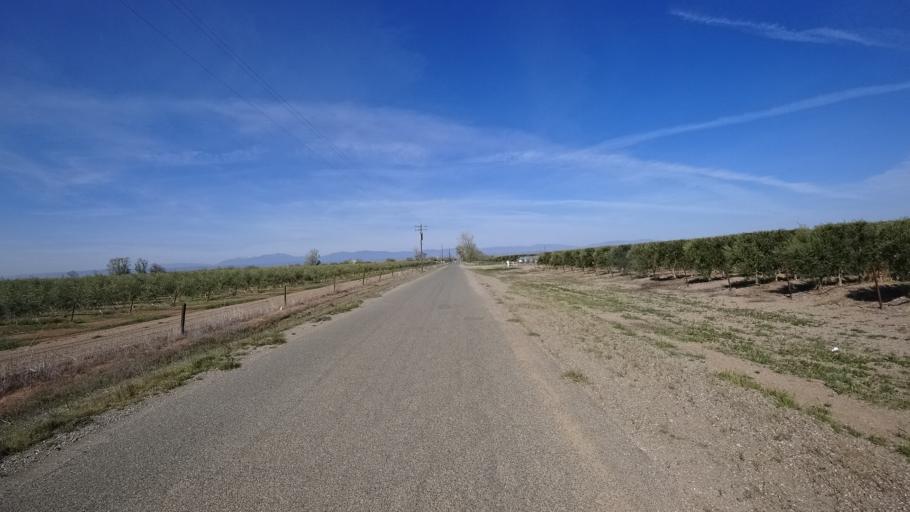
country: US
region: California
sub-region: Glenn County
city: Willows
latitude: 39.6115
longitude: -122.2397
